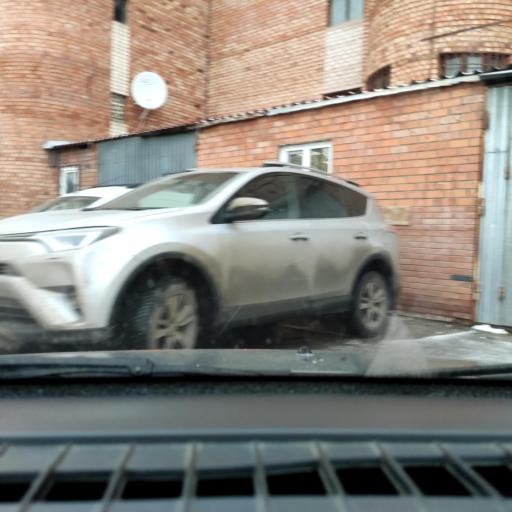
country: RU
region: Samara
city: Tol'yatti
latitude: 53.5456
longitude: 49.2910
